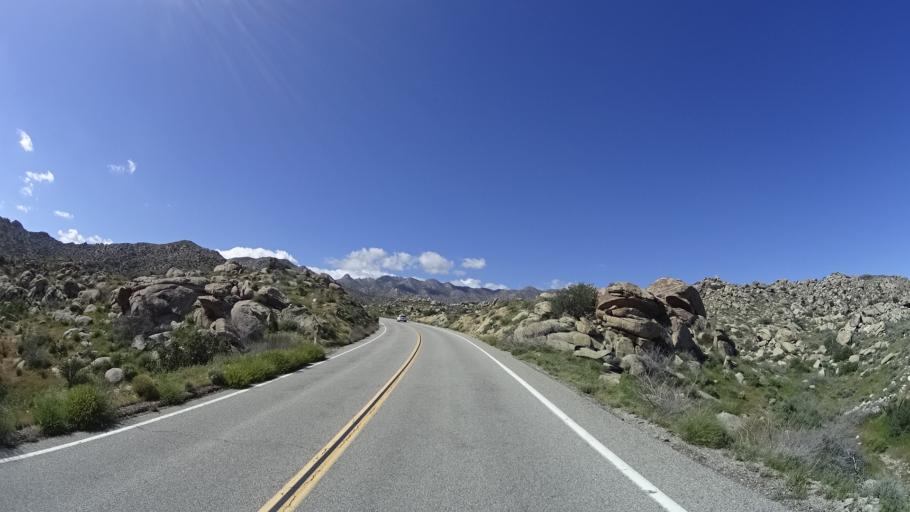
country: US
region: California
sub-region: San Diego County
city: Borrego Springs
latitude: 33.2193
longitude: -116.4536
